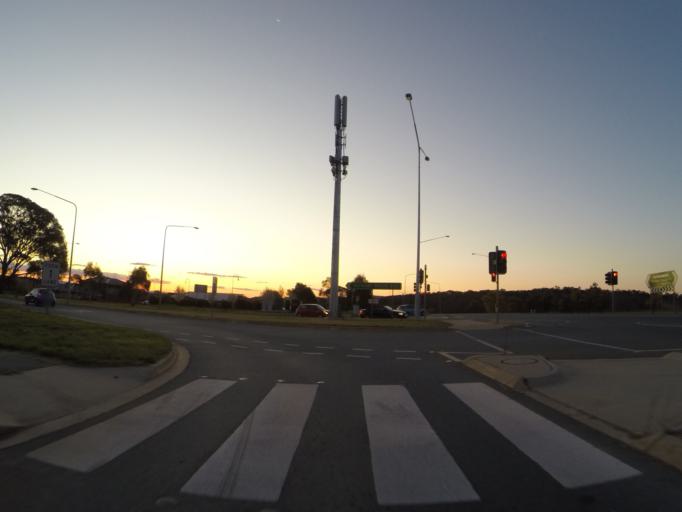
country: AU
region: Australian Capital Territory
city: Kaleen
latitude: -35.1849
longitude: 149.1560
